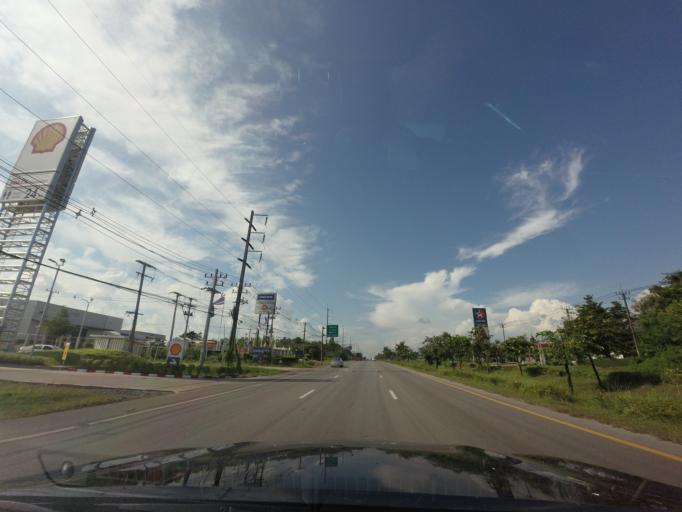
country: TH
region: Nong Khai
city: Nong Khai
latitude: 17.8010
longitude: 102.7614
